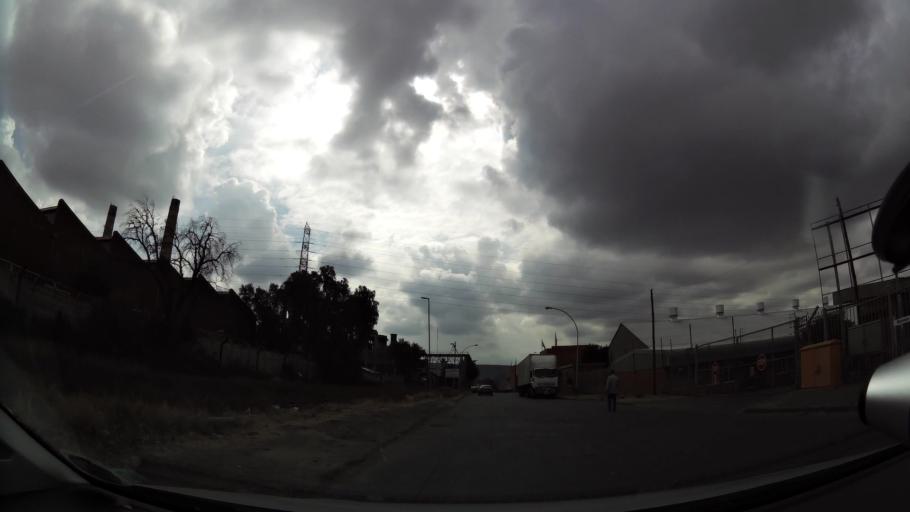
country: ZA
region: Orange Free State
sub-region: Mangaung Metropolitan Municipality
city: Bloemfontein
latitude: -29.1259
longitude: 26.2264
